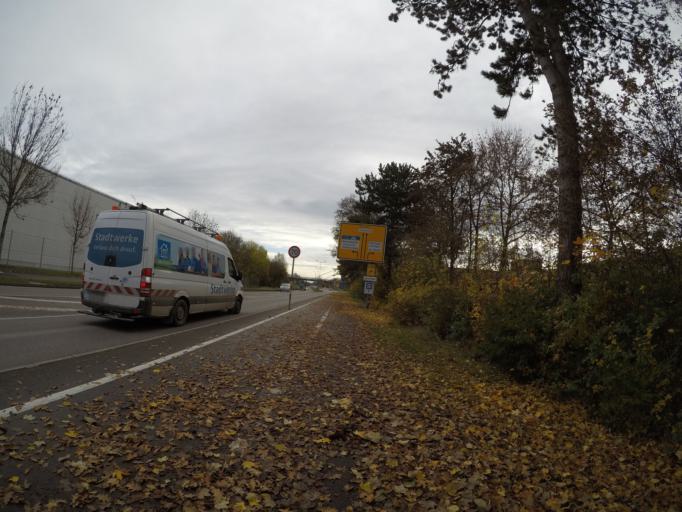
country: DE
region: Baden-Wuerttemberg
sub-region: Tuebingen Region
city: Ulm
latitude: 48.4037
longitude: 9.9443
